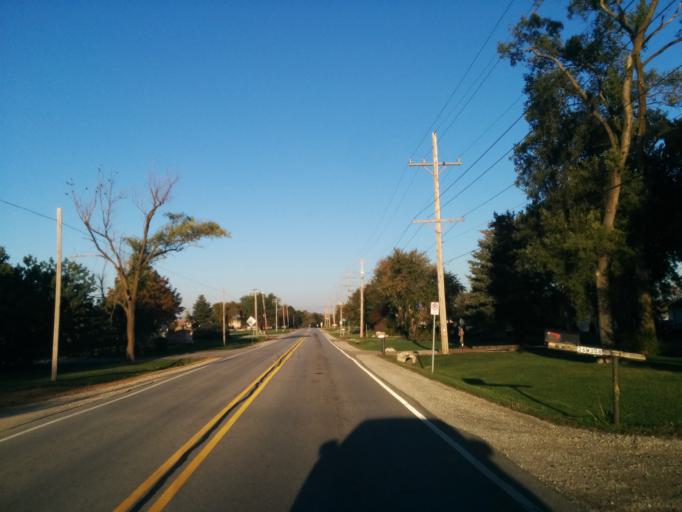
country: US
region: Illinois
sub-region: DuPage County
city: Carol Stream
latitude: 41.9023
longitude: -88.1385
